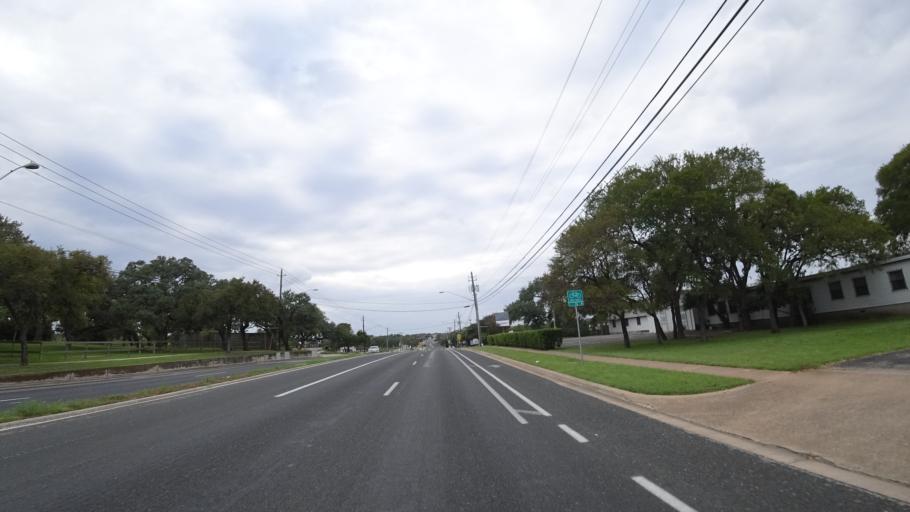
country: US
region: Texas
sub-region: Travis County
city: Rollingwood
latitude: 30.2127
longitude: -97.7920
